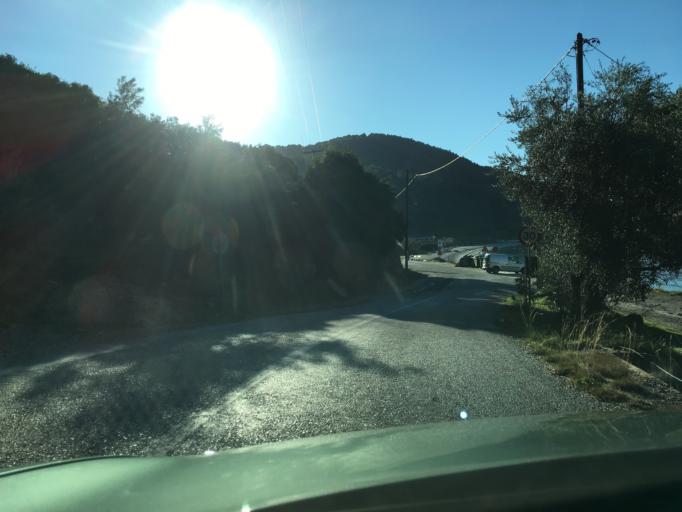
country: GR
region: Thessaly
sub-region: Nomos Magnisias
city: Skopelos
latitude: 39.1129
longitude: 23.6627
